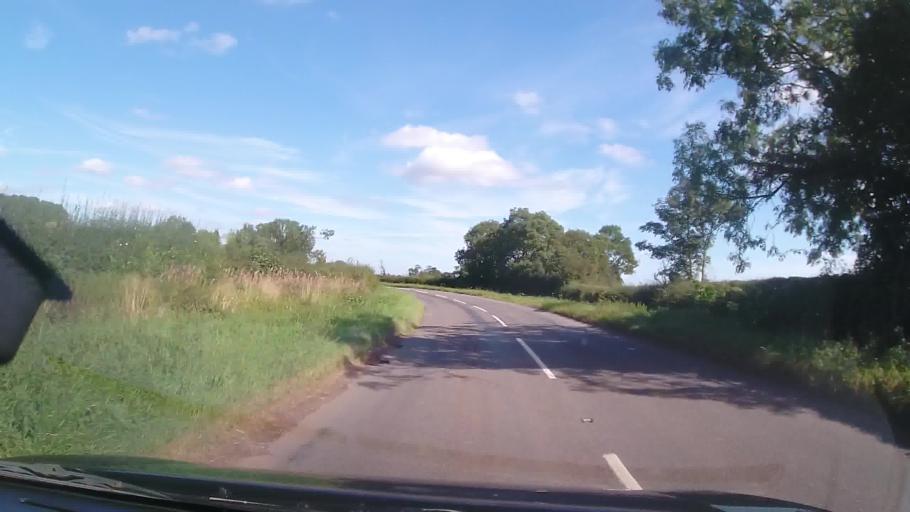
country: GB
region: England
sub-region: Warwickshire
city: Atherstone
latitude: 52.6135
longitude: -1.5069
